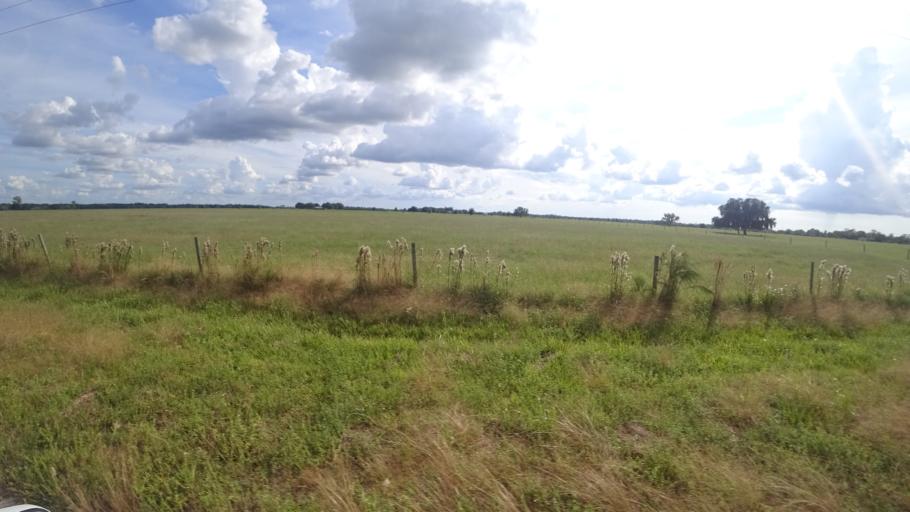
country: US
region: Florida
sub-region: Sarasota County
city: Lake Sarasota
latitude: 27.3391
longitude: -82.1825
